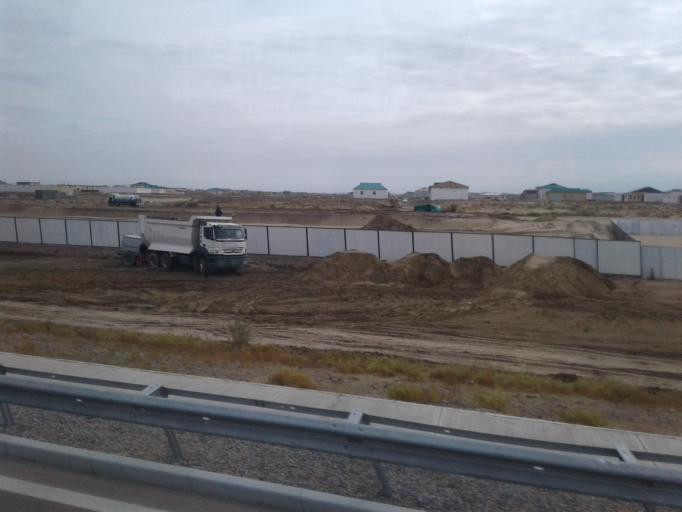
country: TM
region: Lebap
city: Turkmenabat
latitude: 38.9812
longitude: 63.5553
